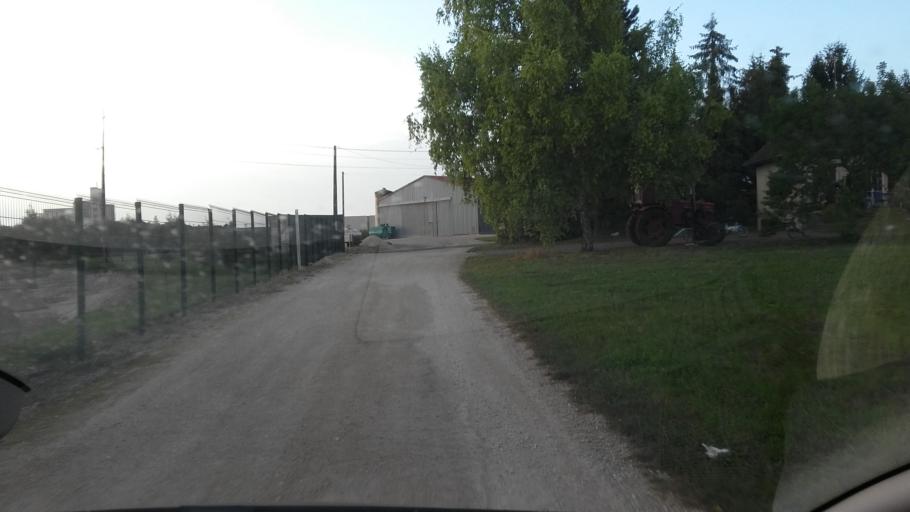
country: FR
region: Champagne-Ardenne
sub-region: Departement de la Marne
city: Fere-Champenoise
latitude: 48.7591
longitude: 3.9917
